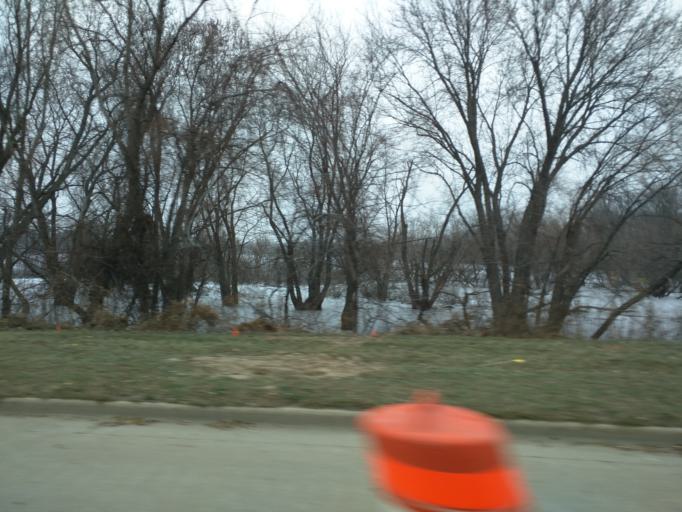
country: US
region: Wisconsin
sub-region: La Crosse County
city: North La Crosse
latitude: 43.8414
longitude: -91.2561
